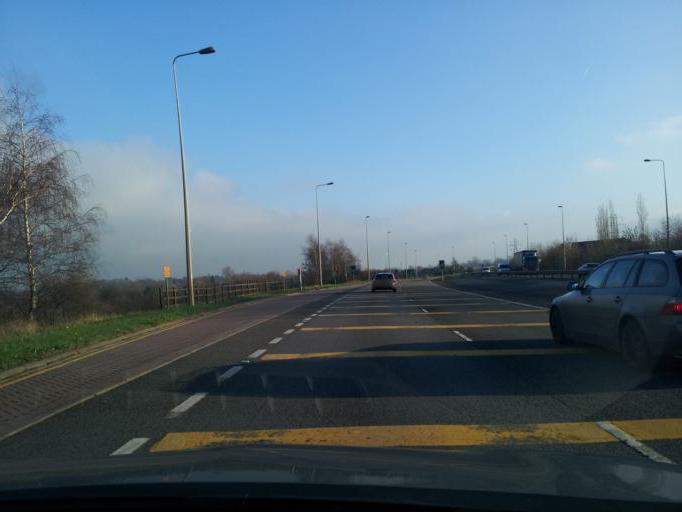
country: GB
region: England
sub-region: Staffordshire
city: Uttoxeter
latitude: 52.9089
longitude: -1.8564
